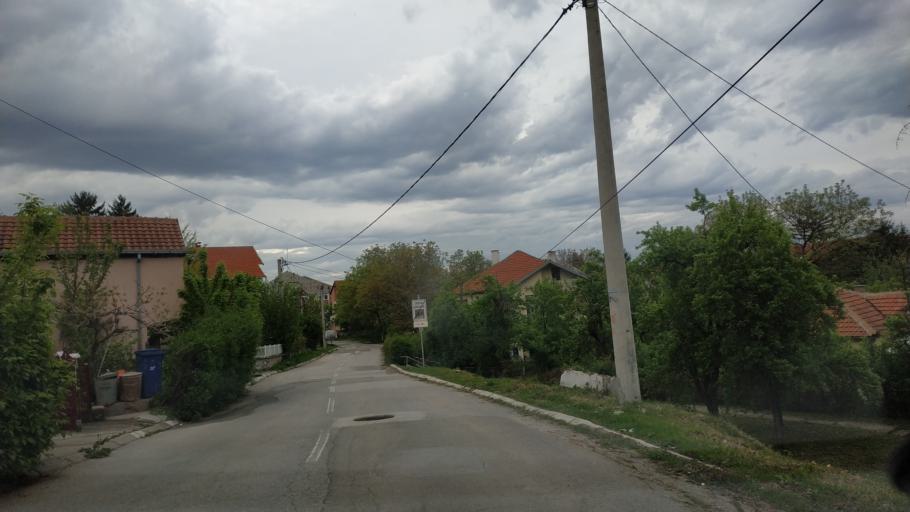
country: RS
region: Central Serbia
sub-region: Zajecarski Okrug
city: Soko Banja
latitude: 43.6424
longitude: 21.8709
